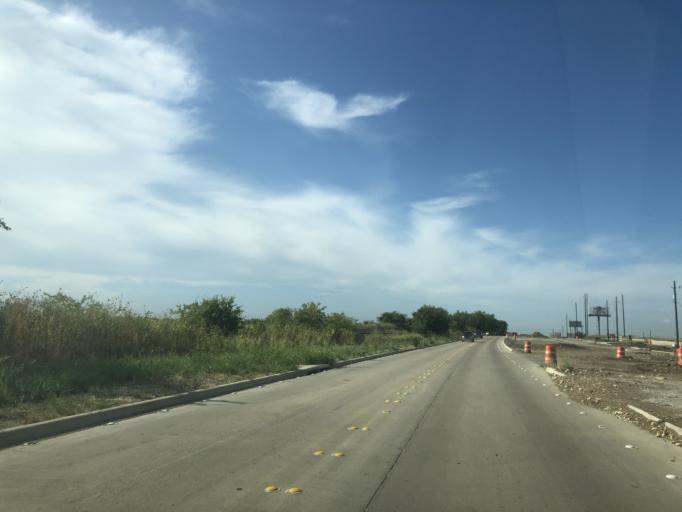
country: US
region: Texas
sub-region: Denton County
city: Justin
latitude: 33.0666
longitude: -97.2959
